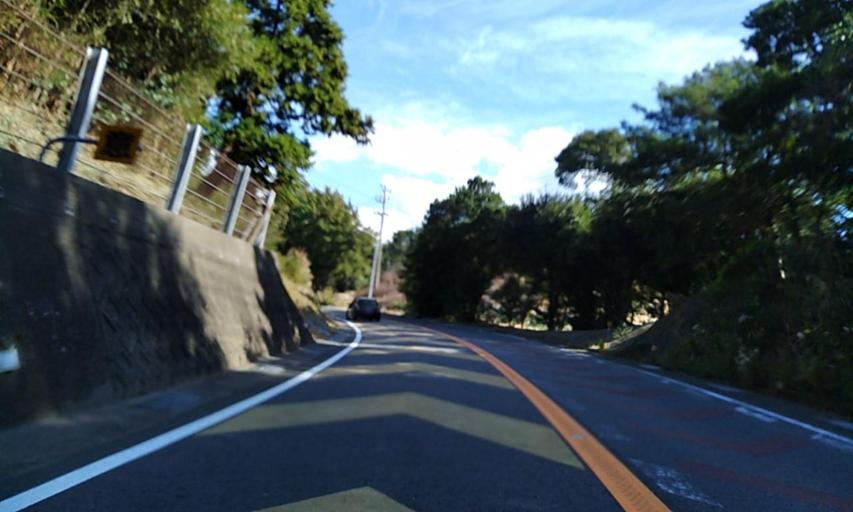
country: JP
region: Wakayama
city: Tanabe
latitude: 33.7801
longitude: 135.2993
